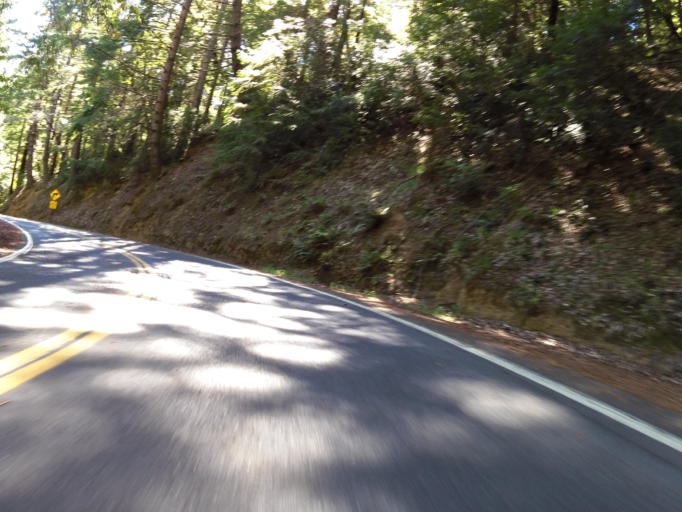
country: US
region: California
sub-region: Humboldt County
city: Redway
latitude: 39.7982
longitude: -123.8102
